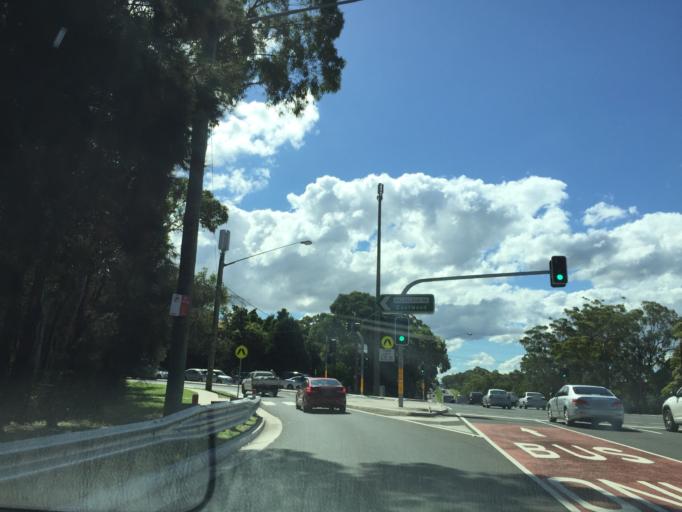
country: AU
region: New South Wales
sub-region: Ryde
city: Marsfield
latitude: -33.7781
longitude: 151.1085
